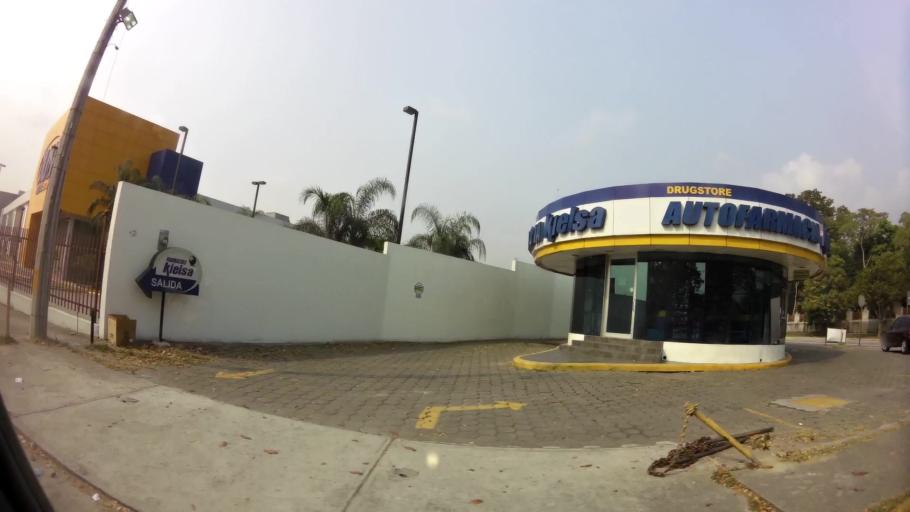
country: HN
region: Cortes
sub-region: San Pedro Sula
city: Pena Blanca
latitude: 15.5255
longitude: -88.0394
